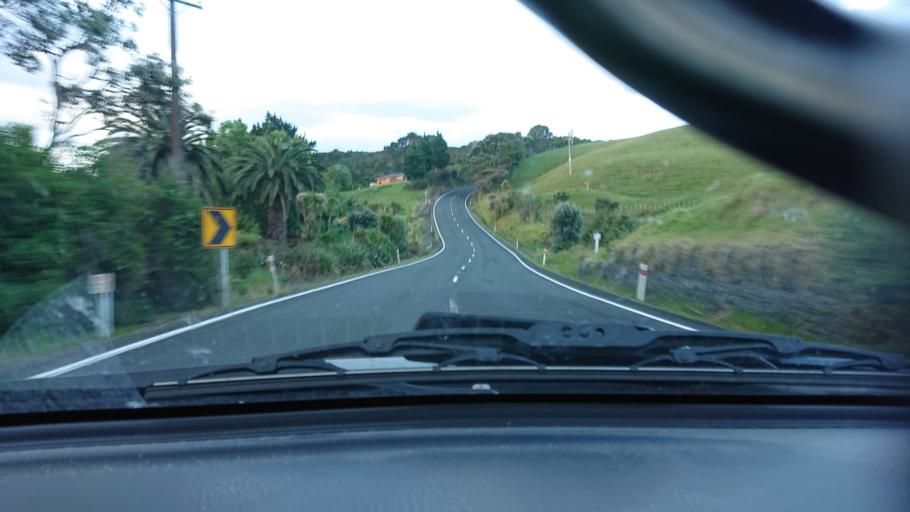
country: NZ
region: Auckland
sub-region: Auckland
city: Wellsford
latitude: -36.4396
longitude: 174.4320
